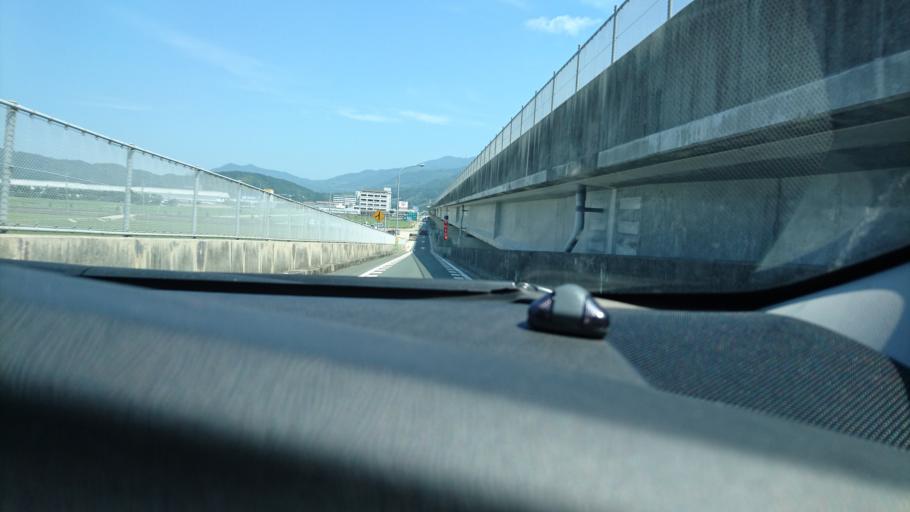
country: JP
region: Ehime
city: Ozu
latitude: 33.5224
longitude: 132.5768
